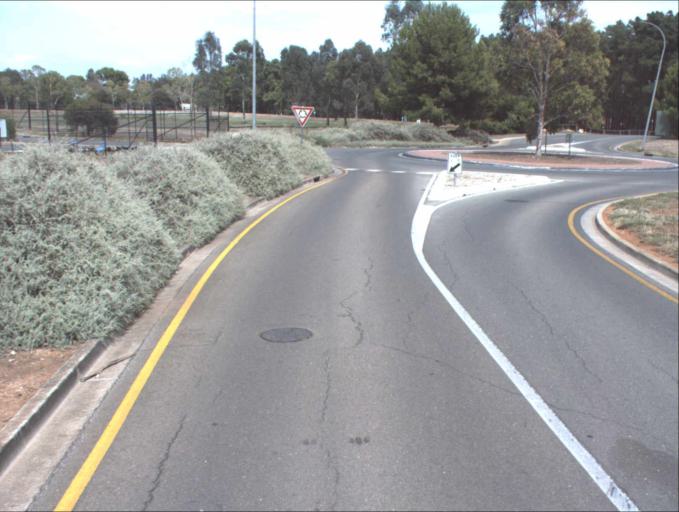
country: AU
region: South Australia
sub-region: Port Adelaide Enfield
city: Enfield
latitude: -34.8414
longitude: 138.6073
